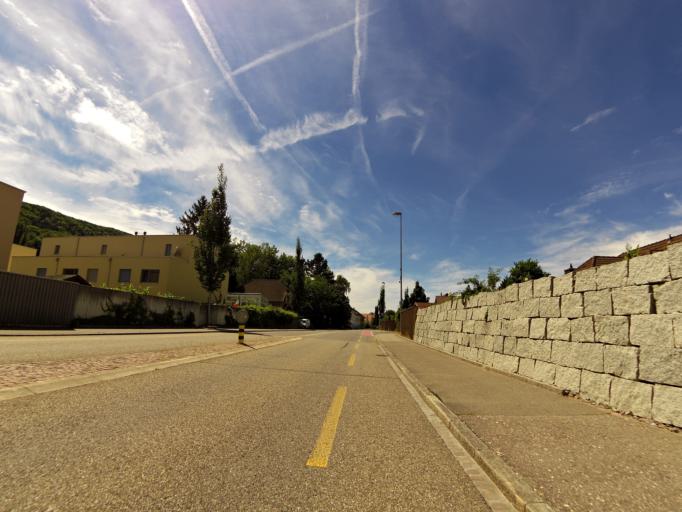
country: CH
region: Aargau
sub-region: Bezirk Rheinfelden
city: Stein
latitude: 47.5417
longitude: 7.9546
